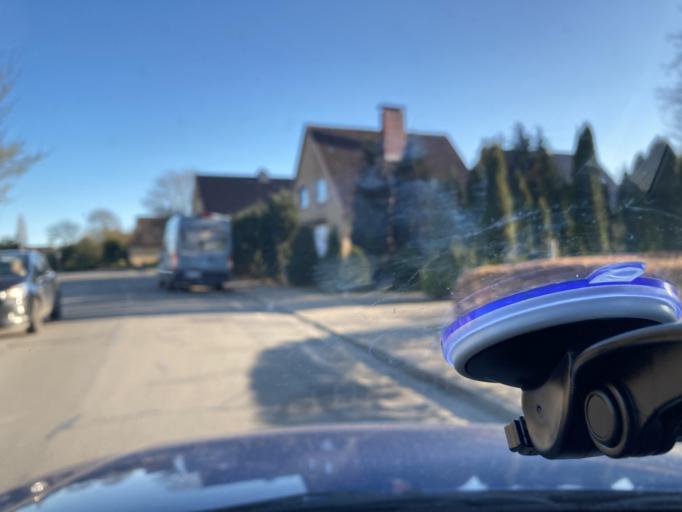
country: DE
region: Schleswig-Holstein
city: Heide
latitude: 54.2052
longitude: 9.1051
